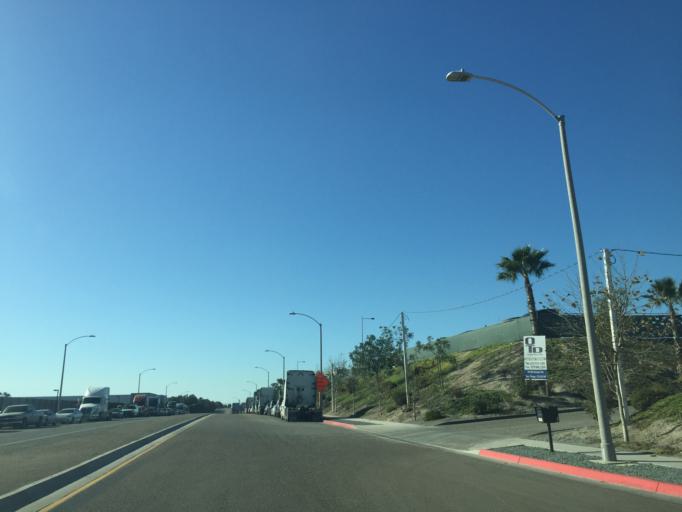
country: MX
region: Baja California
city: Tijuana
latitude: 32.5601
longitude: -116.9244
